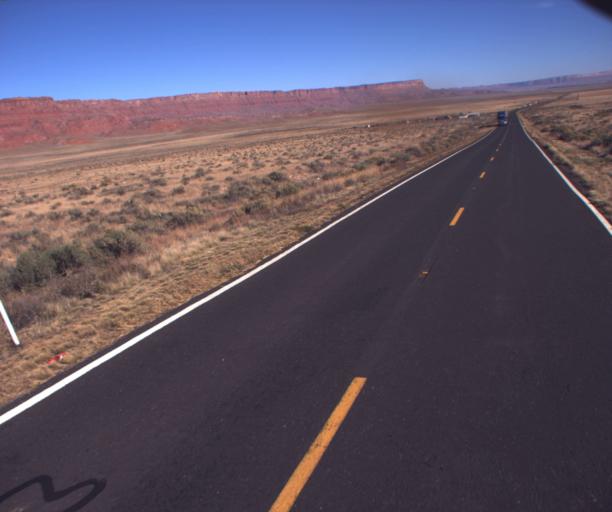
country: US
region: Arizona
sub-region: Coconino County
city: Fredonia
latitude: 36.7329
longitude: -112.0537
